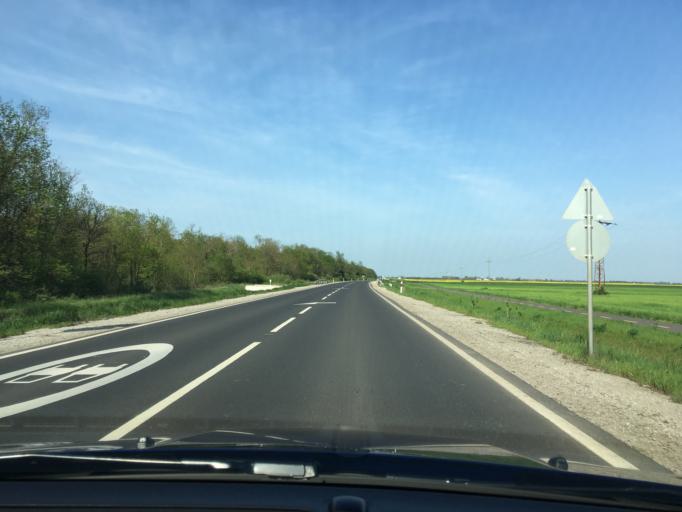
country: HU
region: Bekes
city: Csorvas
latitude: 46.6417
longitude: 20.8888
